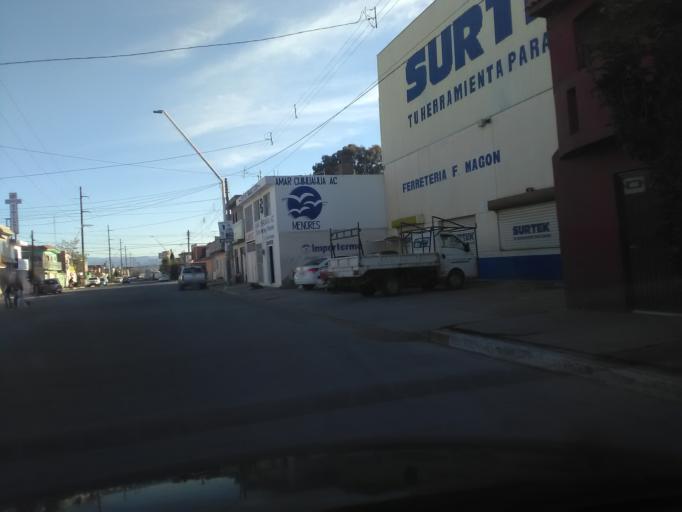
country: MX
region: Durango
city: Victoria de Durango
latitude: 24.0227
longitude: -104.6331
